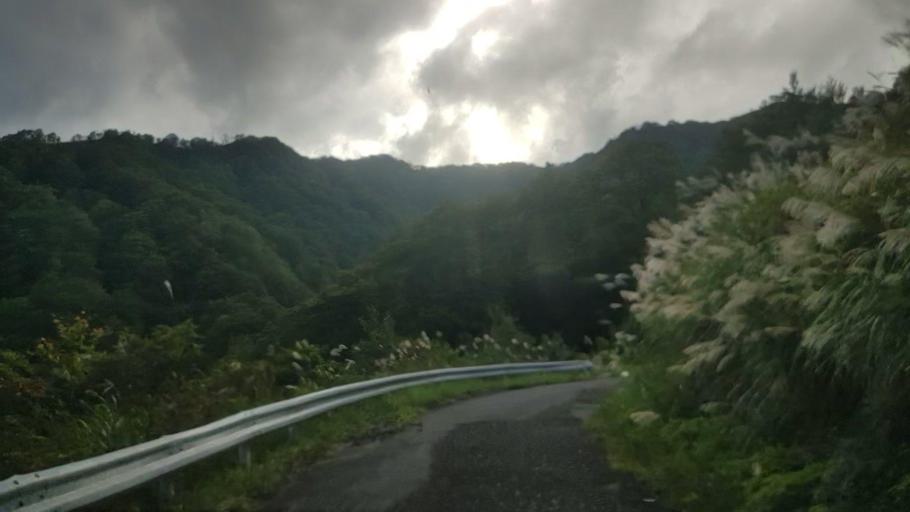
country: JP
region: Toyama
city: Yatsuomachi-higashikumisaka
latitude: 36.3445
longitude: 137.0742
